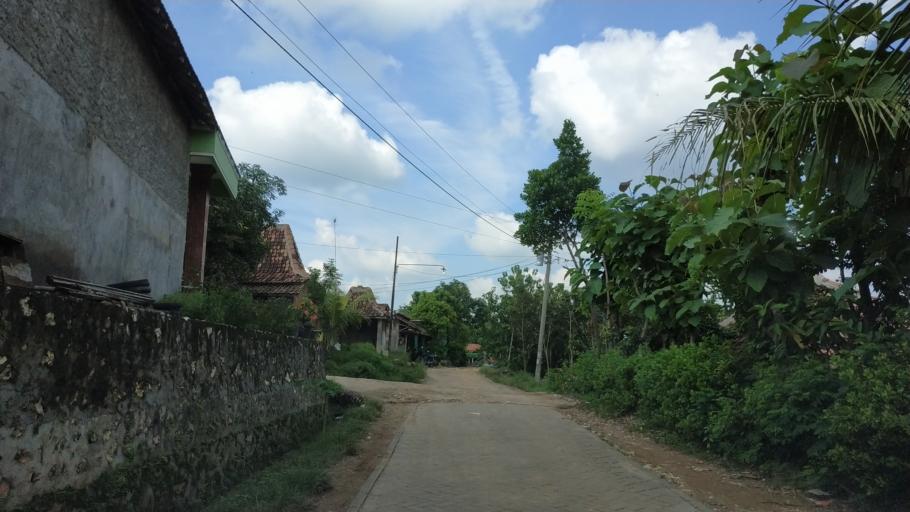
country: ID
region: Central Java
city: Guyangan
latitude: -7.0051
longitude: 111.1123
